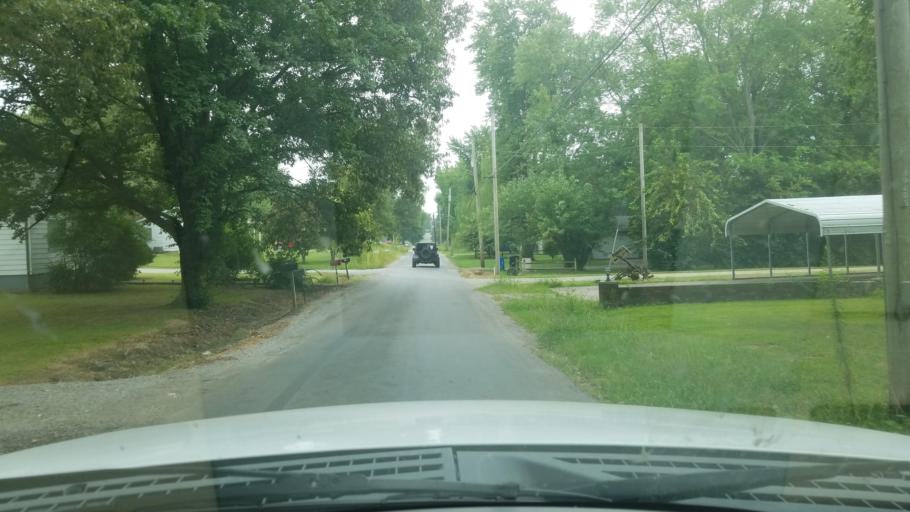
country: US
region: Illinois
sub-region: Saline County
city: Eldorado
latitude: 37.8216
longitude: -88.4477
